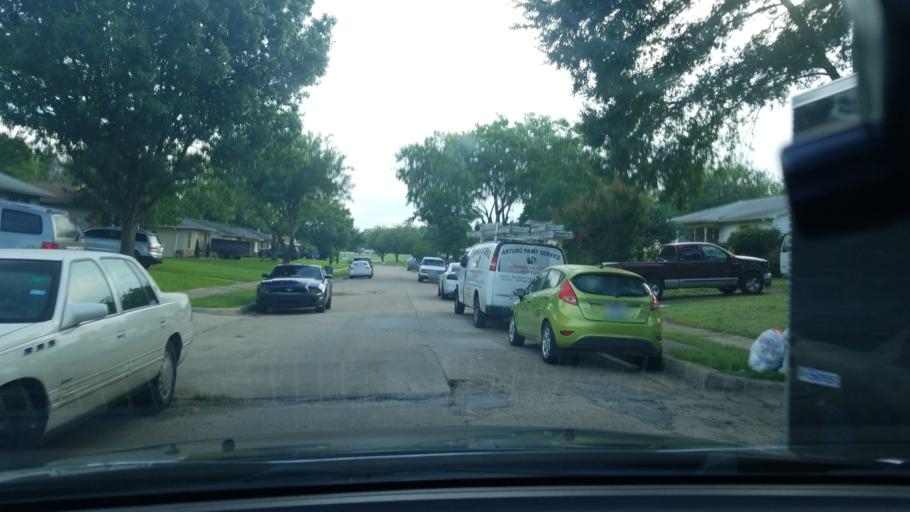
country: US
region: Texas
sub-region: Dallas County
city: Mesquite
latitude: 32.7662
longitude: -96.6370
